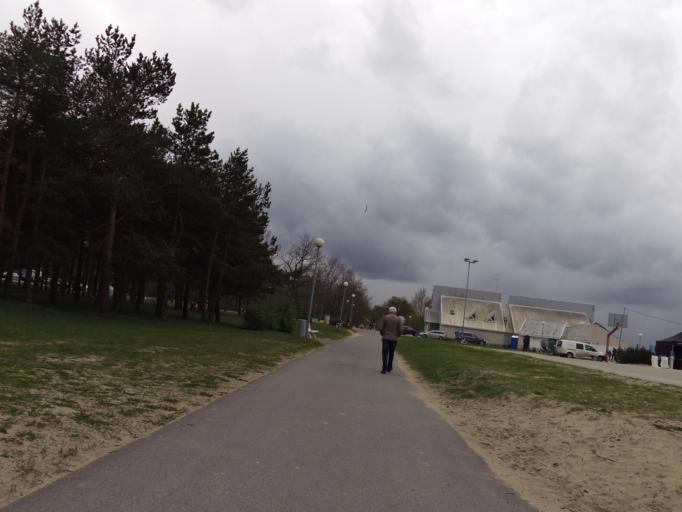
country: EE
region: Harju
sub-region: Tallinna linn
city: Tallinn
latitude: 59.4432
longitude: 24.6855
